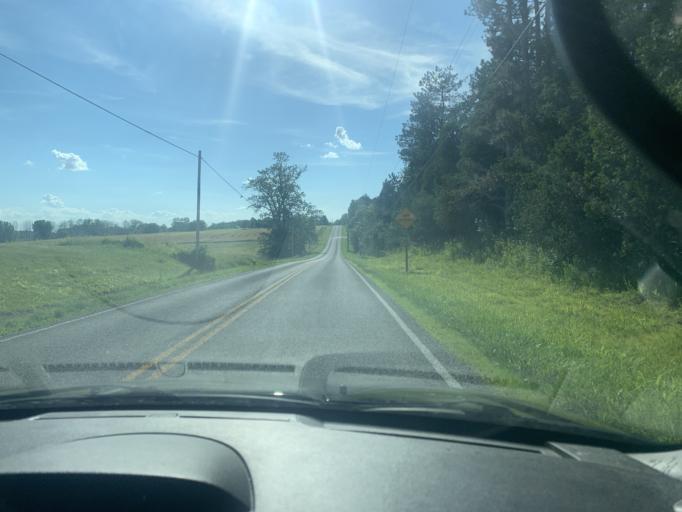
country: US
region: Ohio
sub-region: Logan County
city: Bellefontaine
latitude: 40.3495
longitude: -83.8062
